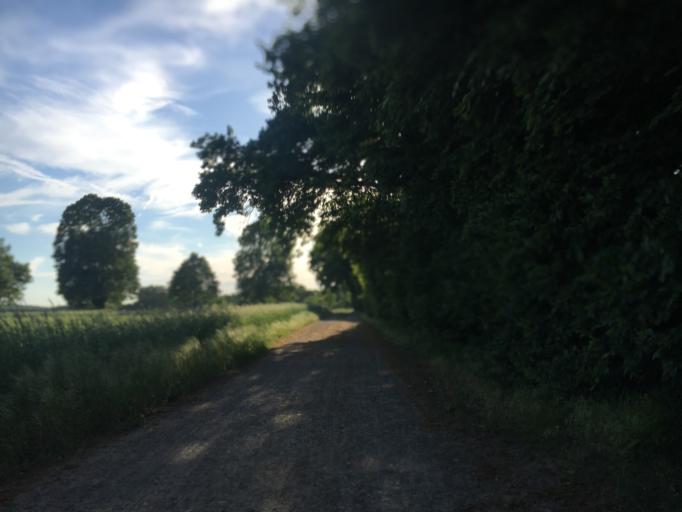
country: DE
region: Brandenburg
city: Potsdam
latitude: 52.4337
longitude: 13.0252
